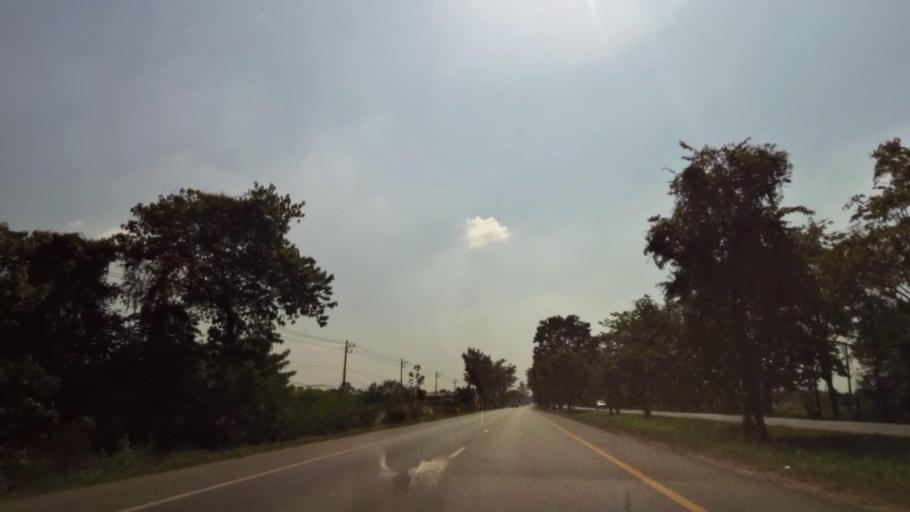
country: TH
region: Phichit
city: Bueng Na Rang
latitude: 16.1782
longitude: 100.1282
